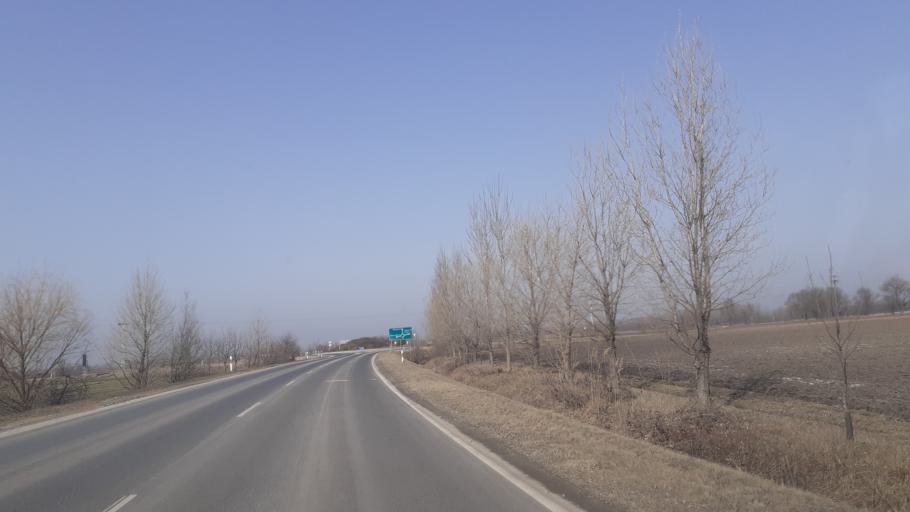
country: HU
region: Pest
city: Bugyi
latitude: 47.2204
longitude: 19.1296
